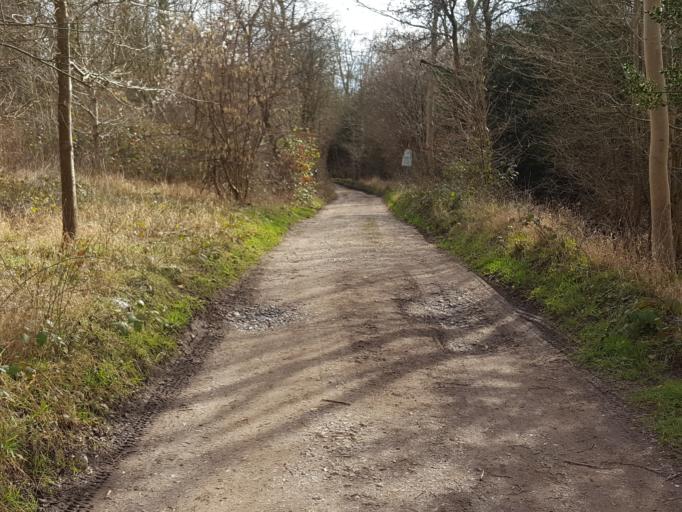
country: GB
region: England
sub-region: Buckinghamshire
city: High Wycombe
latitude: 51.6524
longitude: -0.8100
